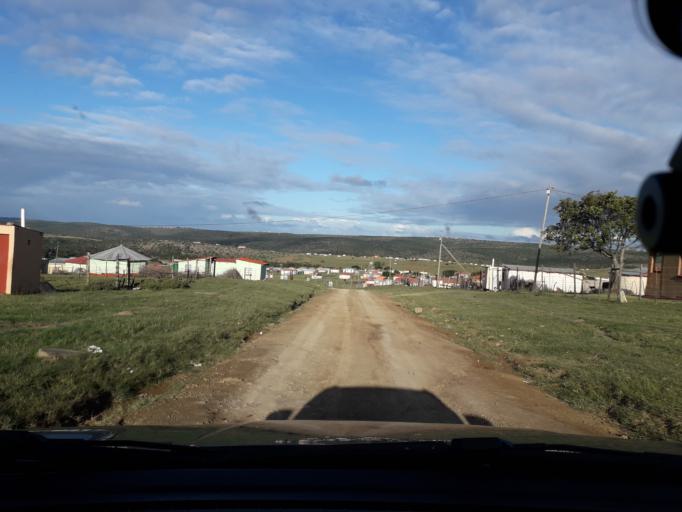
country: ZA
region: Eastern Cape
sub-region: Buffalo City Metropolitan Municipality
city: Bhisho
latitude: -33.1283
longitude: 27.4420
